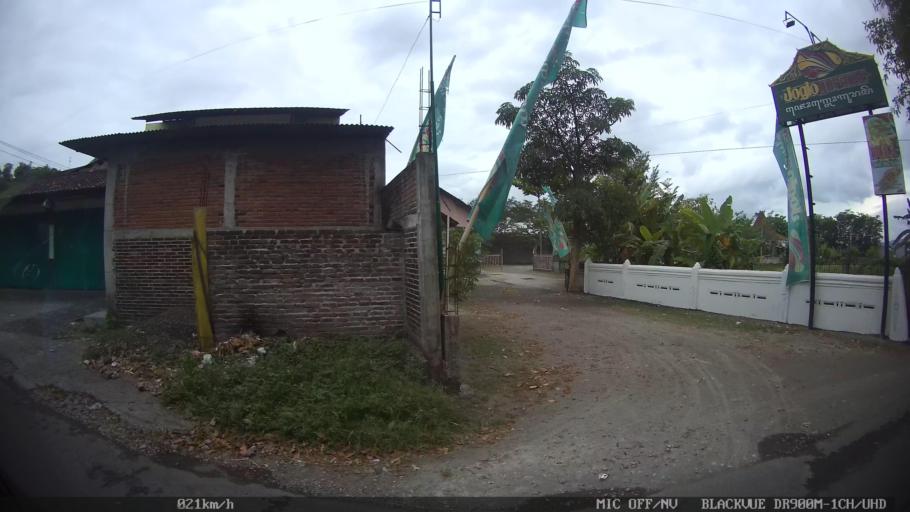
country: ID
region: Daerah Istimewa Yogyakarta
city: Sewon
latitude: -7.8490
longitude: 110.3911
